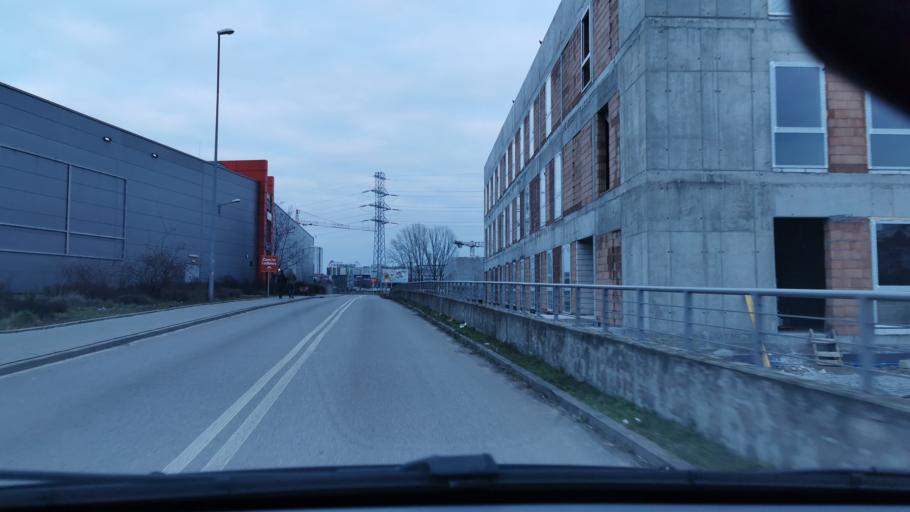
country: PL
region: Masovian Voivodeship
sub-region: Warszawa
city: Praga Poludnie
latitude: 52.2317
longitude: 21.0927
